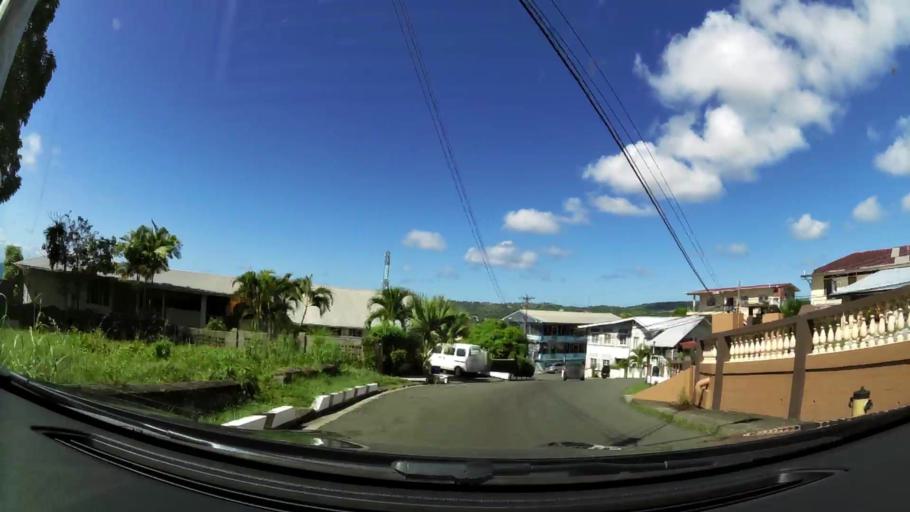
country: TT
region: Tobago
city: Scarborough
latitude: 11.1810
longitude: -60.7321
